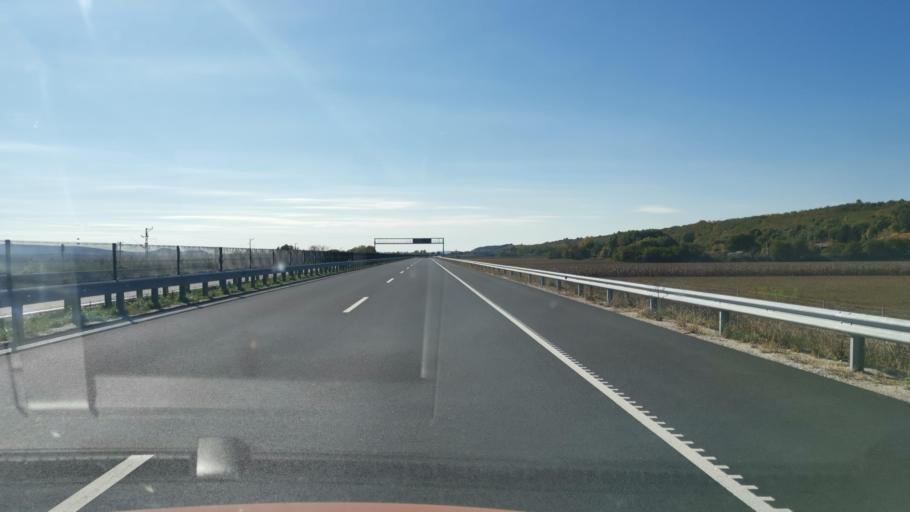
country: HU
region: Borsod-Abauj-Zemplen
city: Gonc
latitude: 48.4406
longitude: 21.1895
